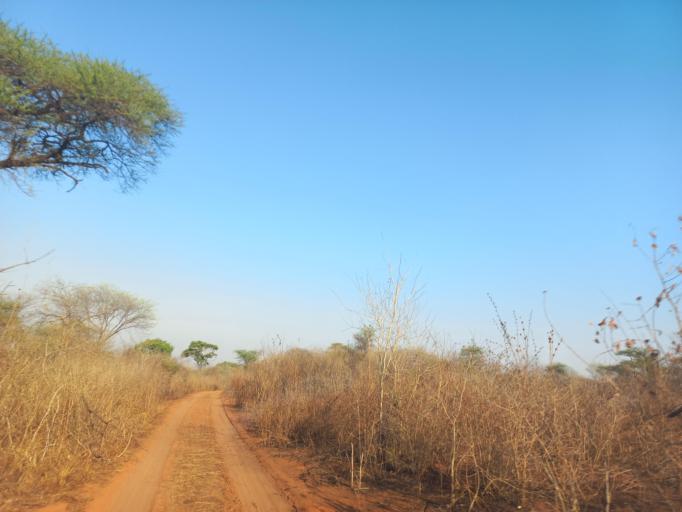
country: ZM
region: Lusaka
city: Luangwa
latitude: -15.4189
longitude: 30.2583
